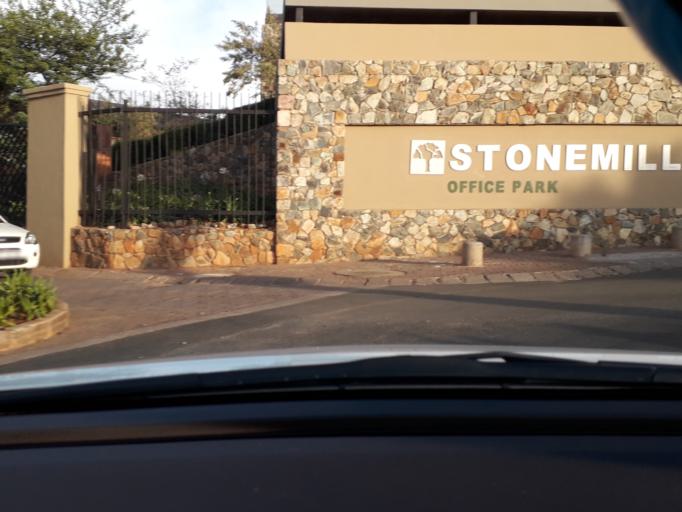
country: ZA
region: Gauteng
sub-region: City of Johannesburg Metropolitan Municipality
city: Johannesburg
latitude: -26.1321
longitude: 27.9780
